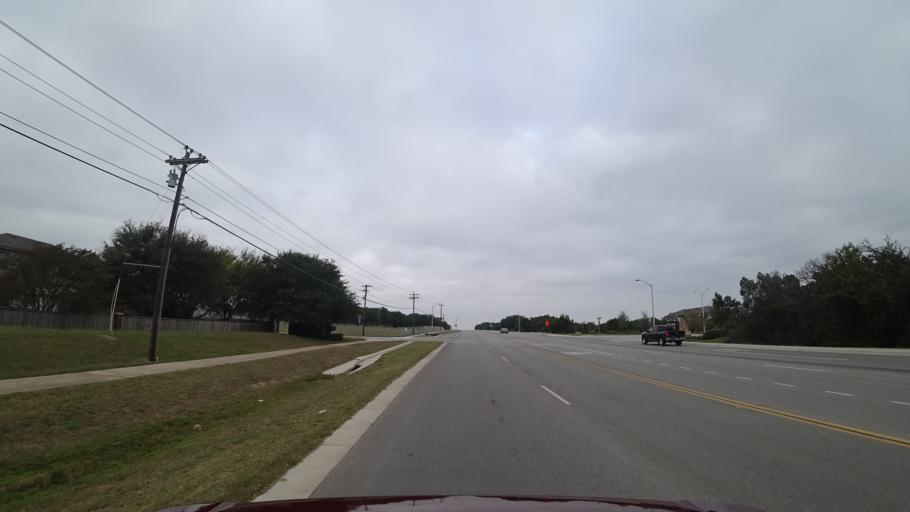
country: US
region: Texas
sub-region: Williamson County
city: Cedar Park
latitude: 30.5234
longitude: -97.8425
